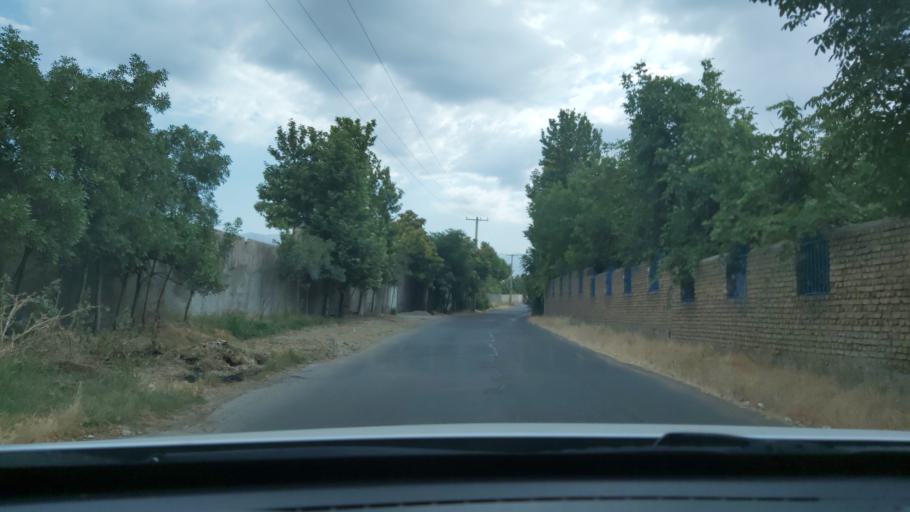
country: IR
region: Alborz
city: Hashtgerd
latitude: 35.9506
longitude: 50.7742
